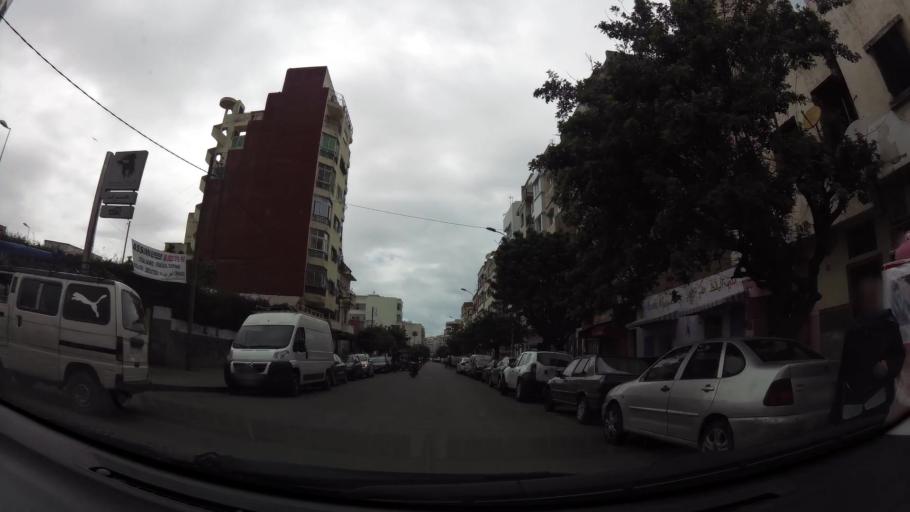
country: MA
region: Grand Casablanca
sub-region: Casablanca
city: Casablanca
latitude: 33.6002
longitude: -7.6295
